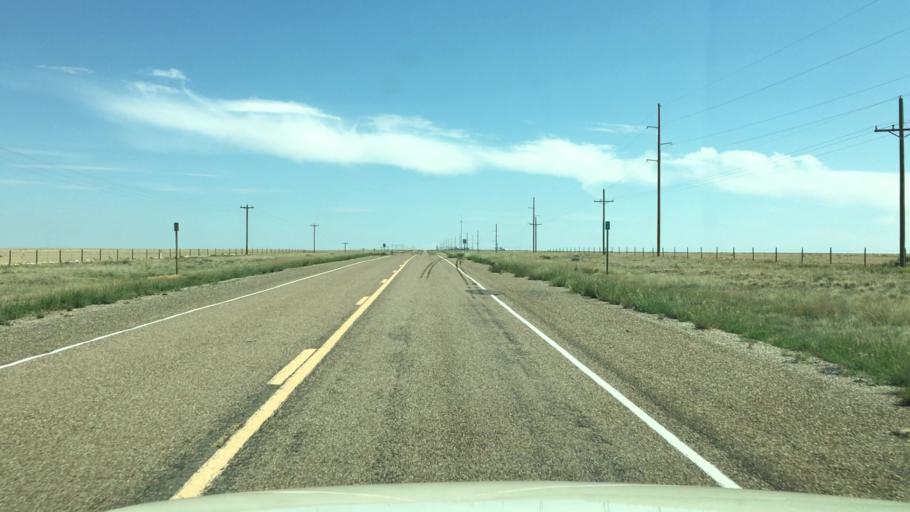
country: US
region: New Mexico
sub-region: Chaves County
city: Roswell
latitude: 33.9452
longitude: -104.5906
